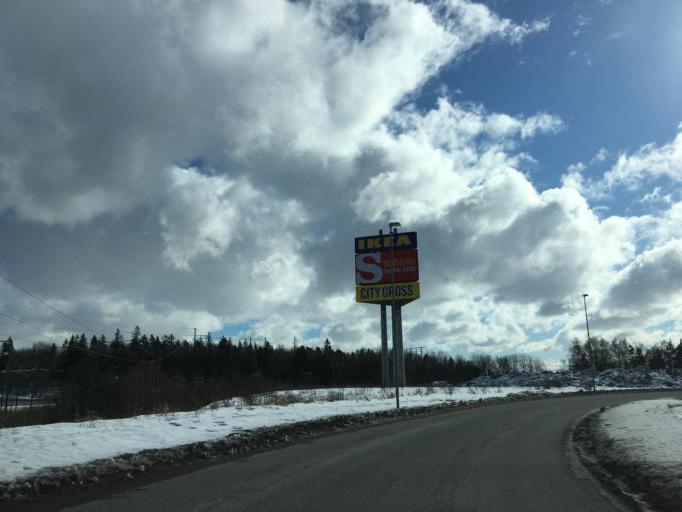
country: SE
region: Vaestmanland
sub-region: Vasteras
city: Vasteras
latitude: 59.6088
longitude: 16.4591
